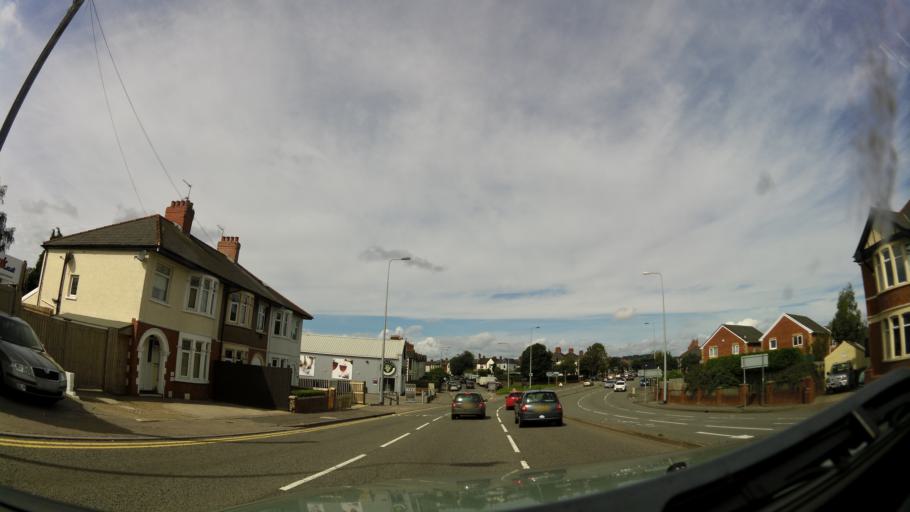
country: GB
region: Wales
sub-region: Cardiff
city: Cardiff
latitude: 51.5086
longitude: -3.2020
